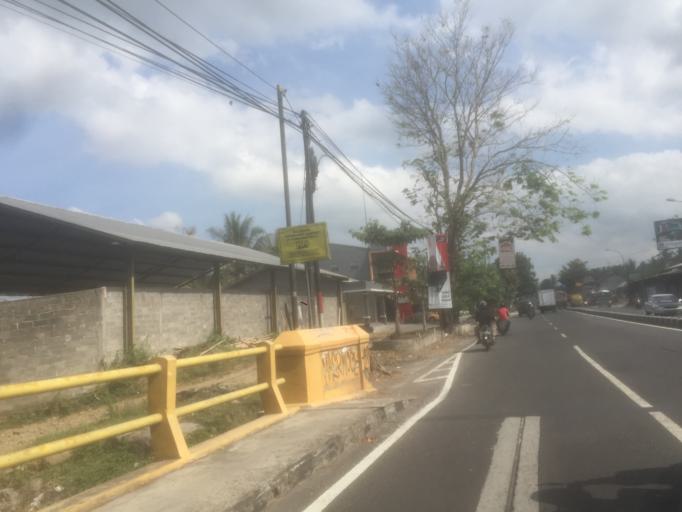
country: ID
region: Daerah Istimewa Yogyakarta
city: Sleman
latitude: -7.6707
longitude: 110.3342
